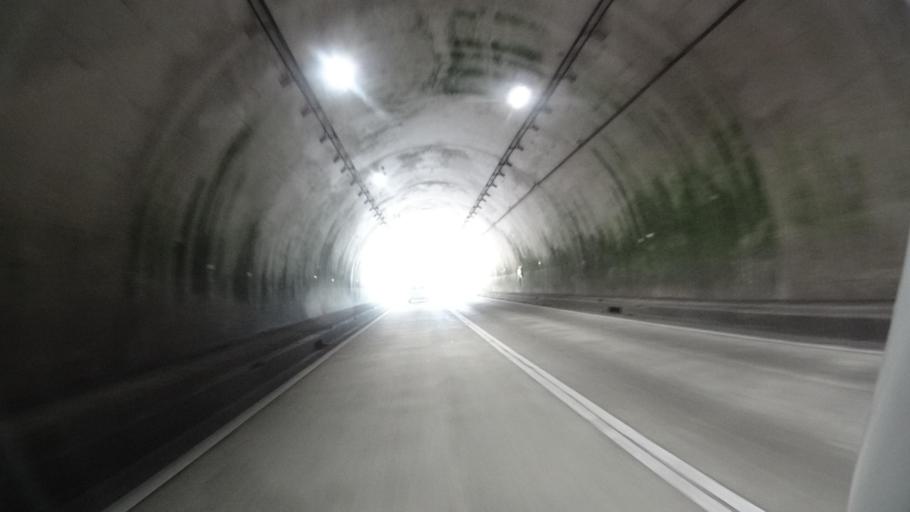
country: JP
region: Kyoto
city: Kameoka
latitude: 35.2219
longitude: 135.5718
